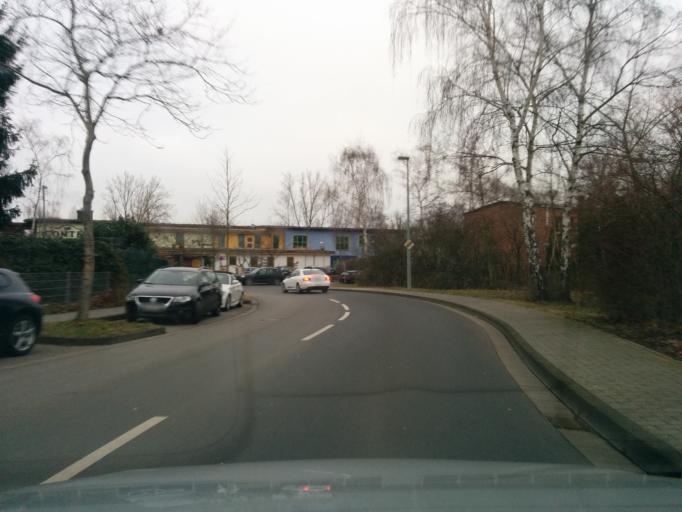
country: DE
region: Rheinland-Pfalz
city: Koblenz
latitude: 50.3653
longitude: 7.5774
